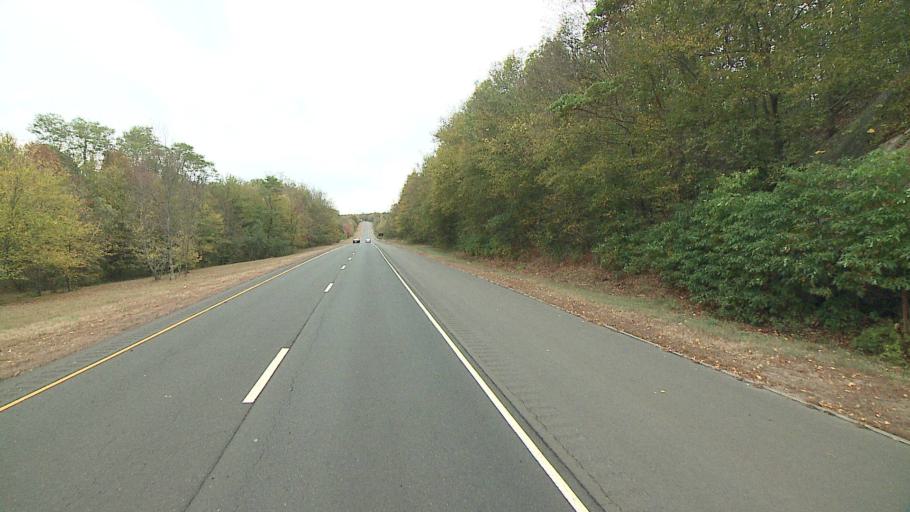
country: US
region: Connecticut
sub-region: Middlesex County
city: East Haddam
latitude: 41.4432
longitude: -72.5194
